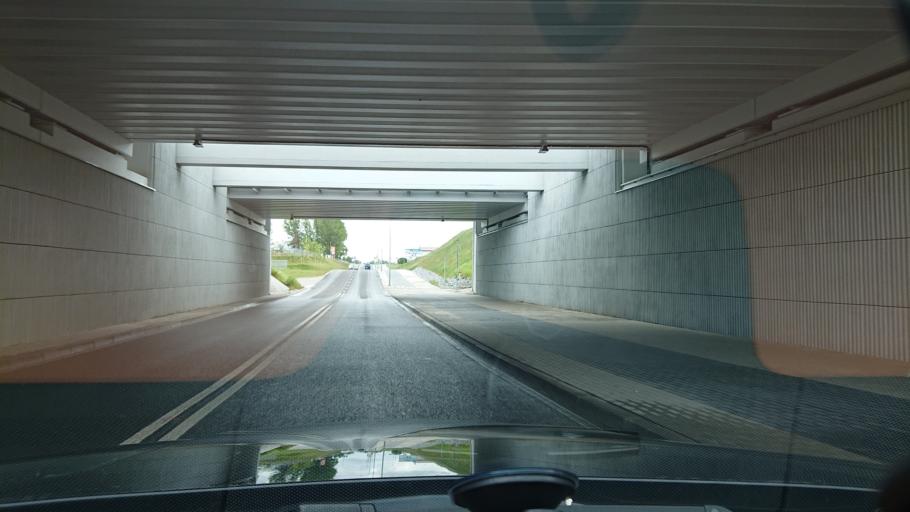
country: PL
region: Greater Poland Voivodeship
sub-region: Powiat gnieznienski
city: Gniezno
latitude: 52.5315
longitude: 17.6214
